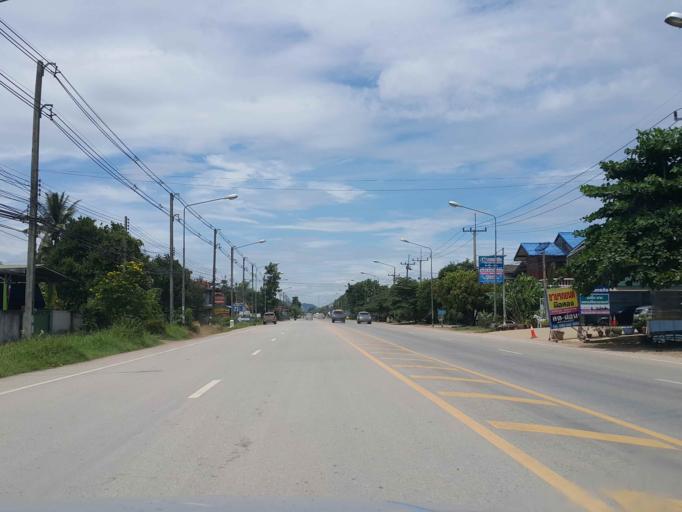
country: TH
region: Sukhothai
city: Ban Na
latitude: 17.0127
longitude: 99.7668
